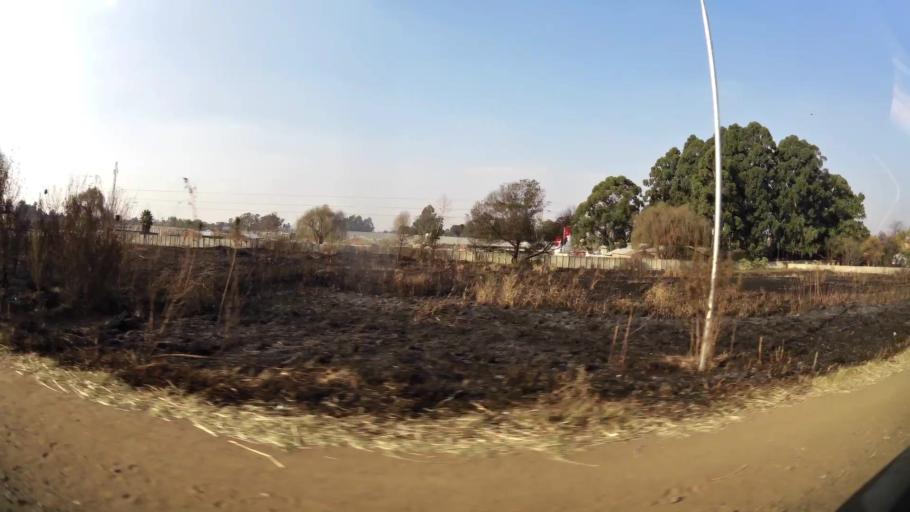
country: ZA
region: Gauteng
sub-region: Ekurhuleni Metropolitan Municipality
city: Benoni
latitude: -26.1370
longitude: 28.3906
